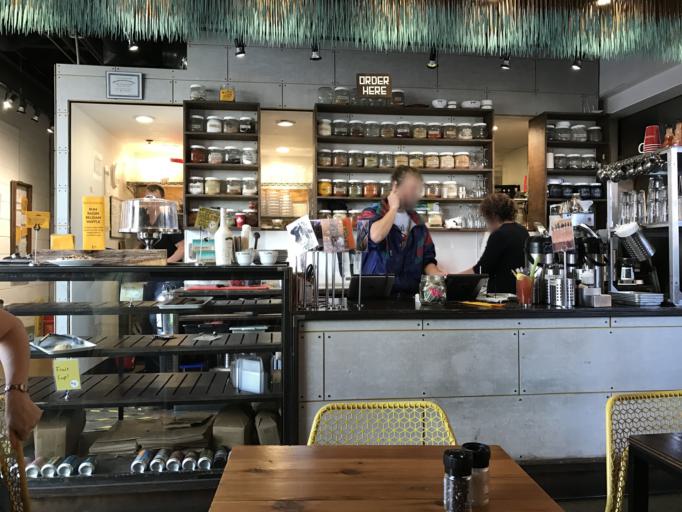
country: US
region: Michigan
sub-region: Washtenaw County
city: Ann Arbor
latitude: 42.2845
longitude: -83.7468
